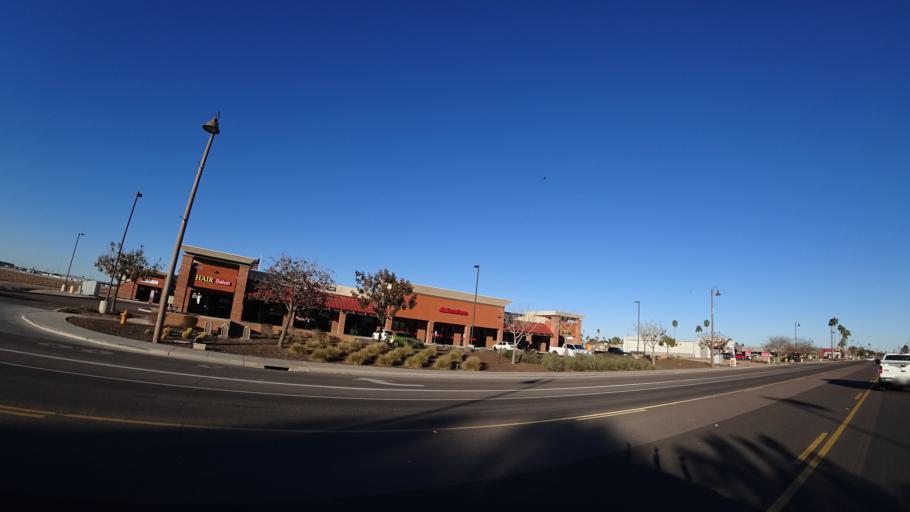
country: US
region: Arizona
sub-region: Maricopa County
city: Tolleson
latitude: 33.4502
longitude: -112.2679
